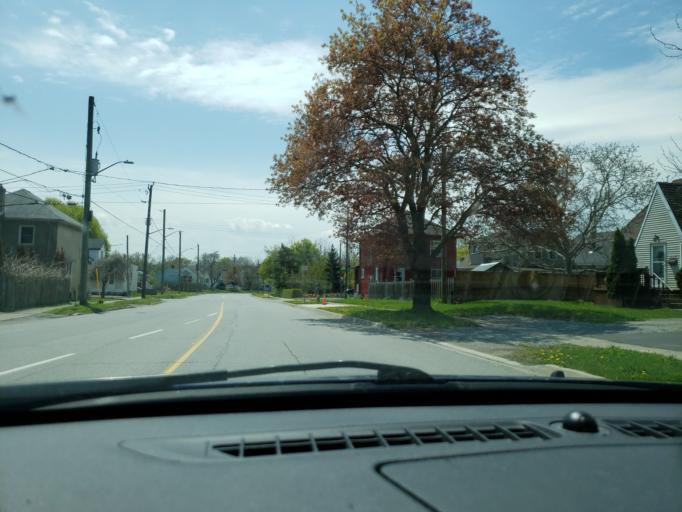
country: CA
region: Ontario
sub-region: Regional Municipality of Niagara
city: St. Catharines
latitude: 43.1609
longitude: -79.2253
